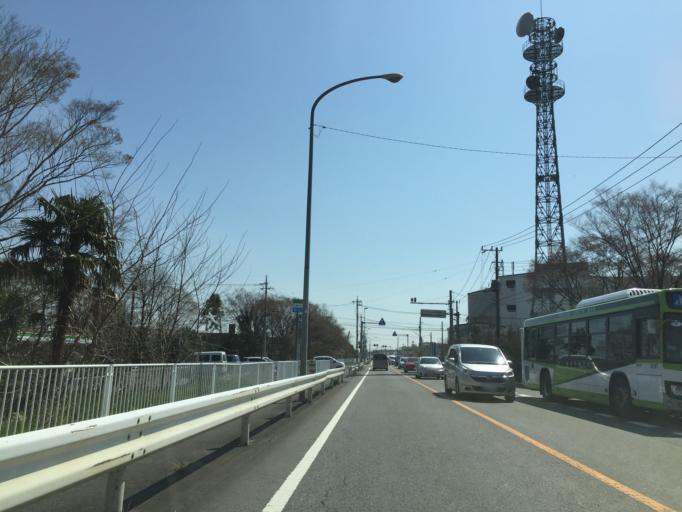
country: JP
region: Saitama
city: Shiki
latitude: 35.8603
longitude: 139.6043
